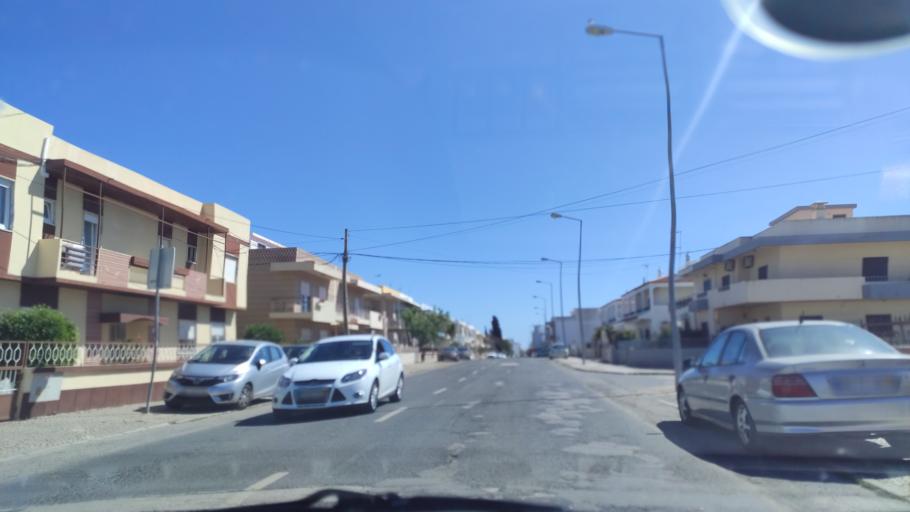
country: PT
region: Faro
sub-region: Olhao
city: Olhao
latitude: 37.0368
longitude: -7.8494
